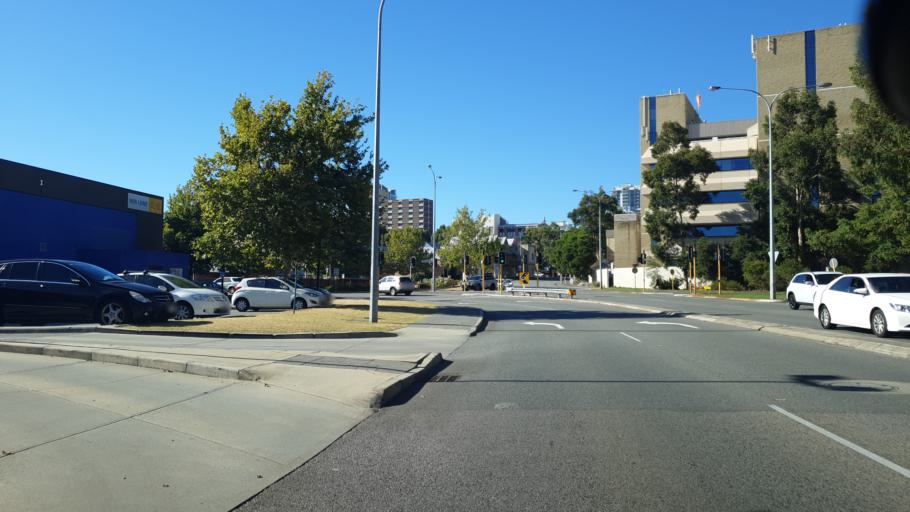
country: AU
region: Western Australia
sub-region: Cambridge
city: Perth
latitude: -31.9524
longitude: 115.8679
